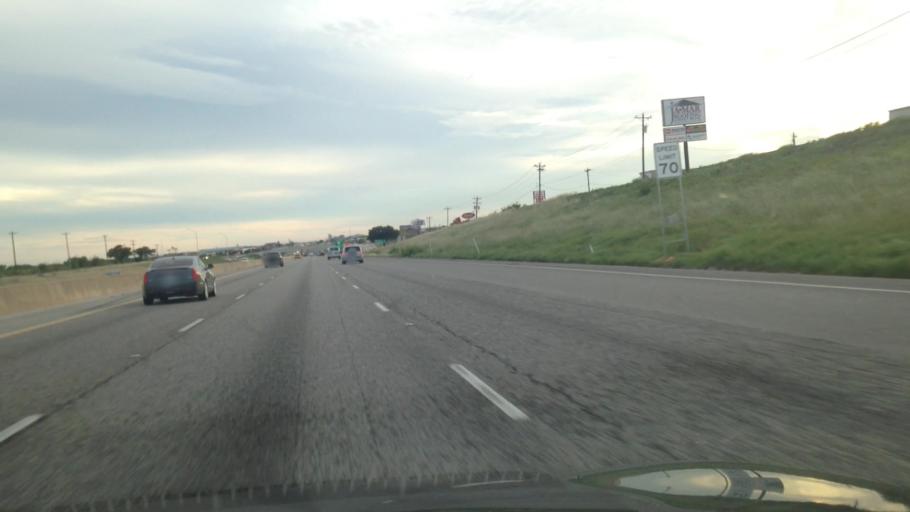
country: US
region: Texas
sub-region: Hays County
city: Buda
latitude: 30.0656
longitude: -97.8308
